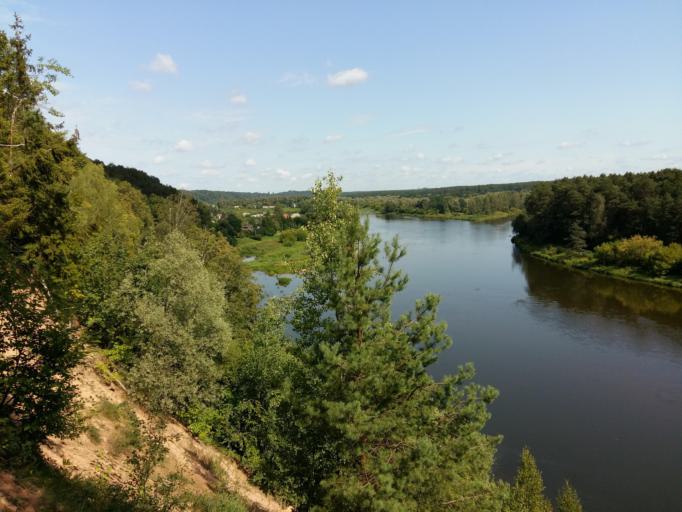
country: LT
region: Kauno apskritis
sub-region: Kauno rajonas
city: Karmelava
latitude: 55.0270
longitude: 24.1079
